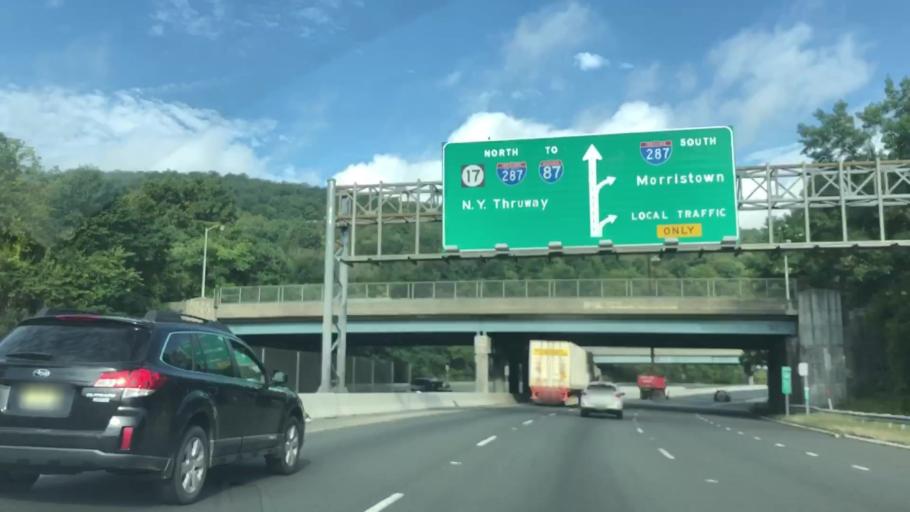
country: US
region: New York
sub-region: Rockland County
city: Suffern
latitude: 41.1019
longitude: -74.1666
